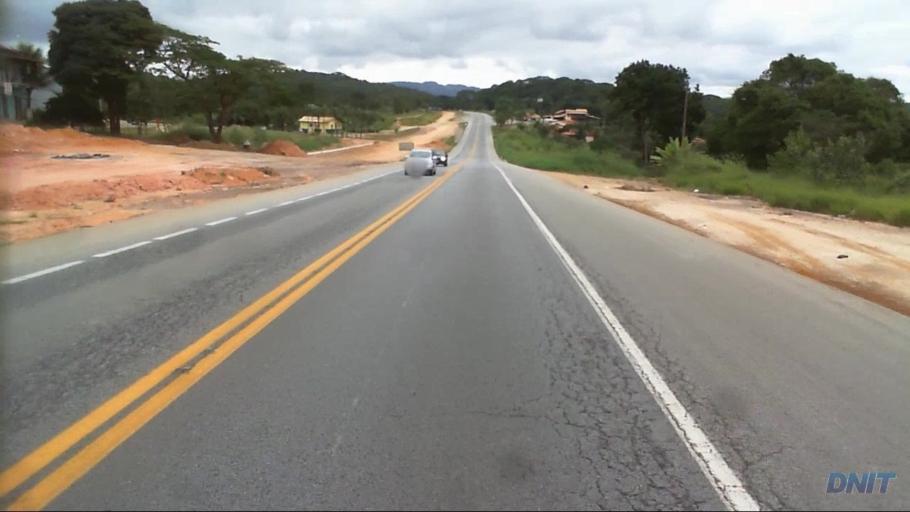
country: BR
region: Minas Gerais
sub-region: Barao De Cocais
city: Barao de Cocais
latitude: -19.7703
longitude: -43.4492
